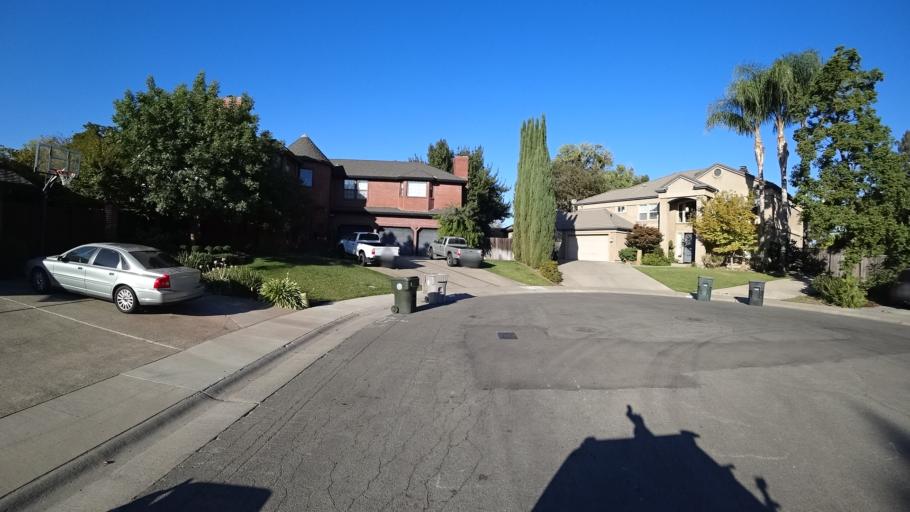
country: US
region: California
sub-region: Yolo County
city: West Sacramento
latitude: 38.5001
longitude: -121.5571
